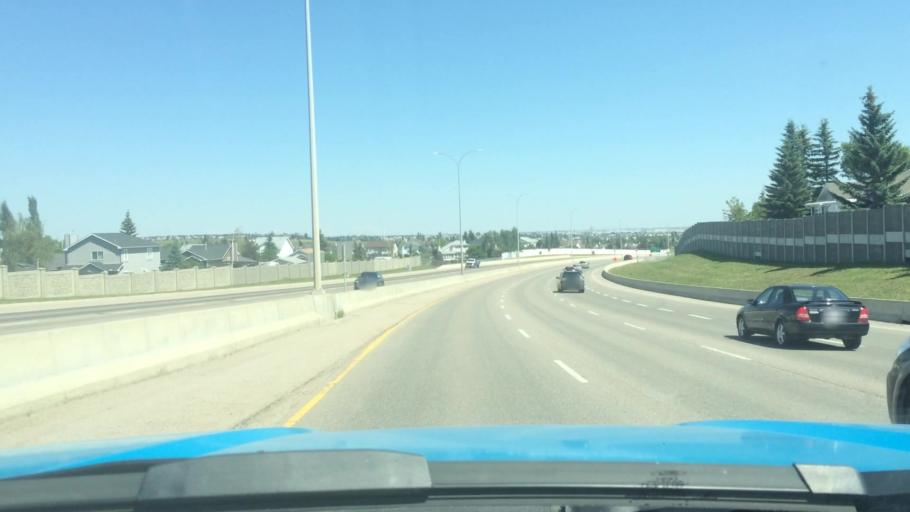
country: CA
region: Alberta
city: Calgary
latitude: 51.1441
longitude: -114.1184
